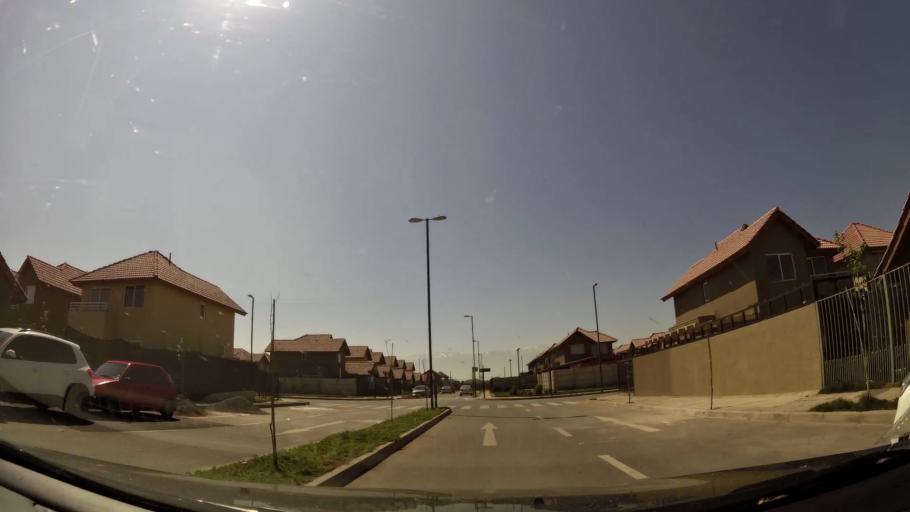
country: CL
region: Santiago Metropolitan
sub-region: Provincia de Chacabuco
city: Chicureo Abajo
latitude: -33.3224
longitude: -70.7563
